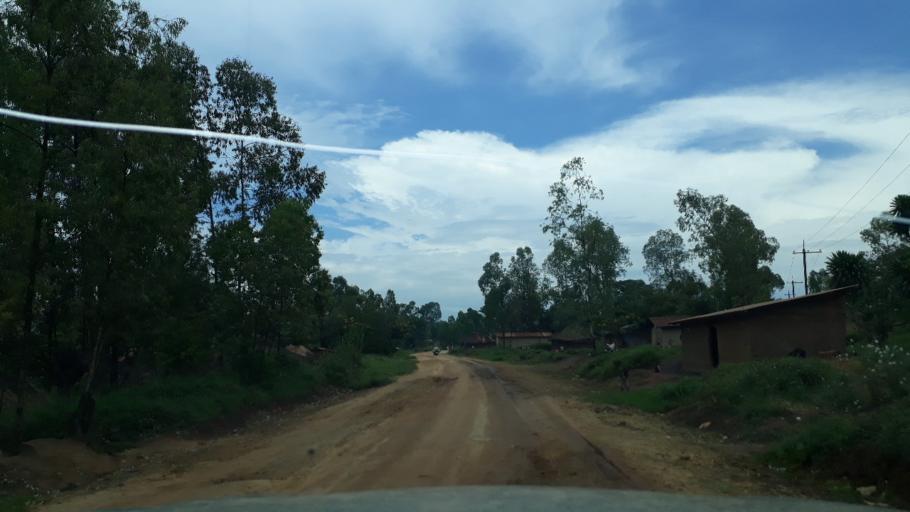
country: CD
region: Eastern Province
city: Bunia
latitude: 1.6641
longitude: 30.2758
